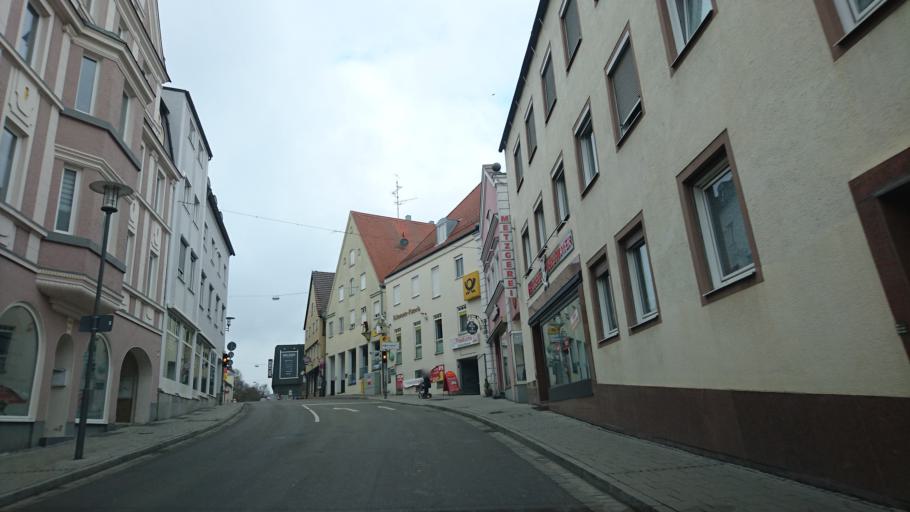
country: DE
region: Bavaria
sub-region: Swabia
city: Dillingen an der Donau
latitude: 48.5773
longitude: 10.4966
